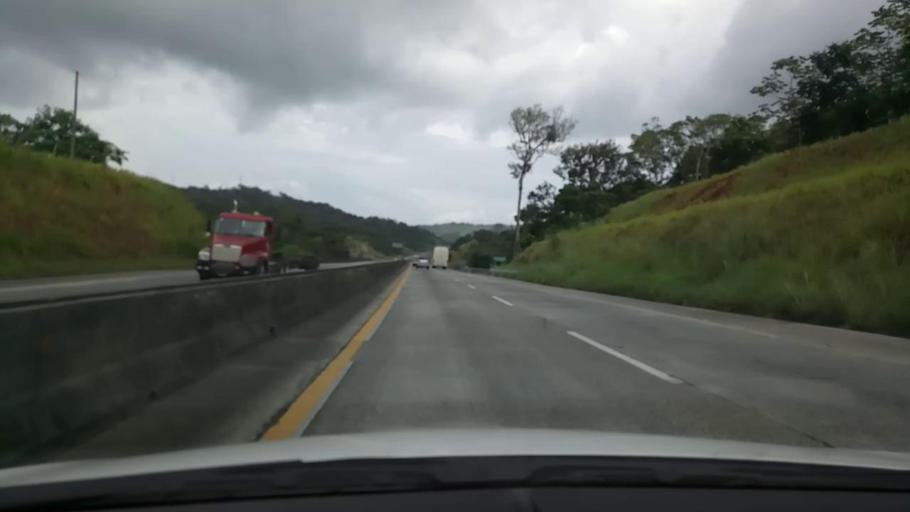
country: PA
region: Colon
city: Gatun
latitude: 9.2826
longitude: -79.7733
